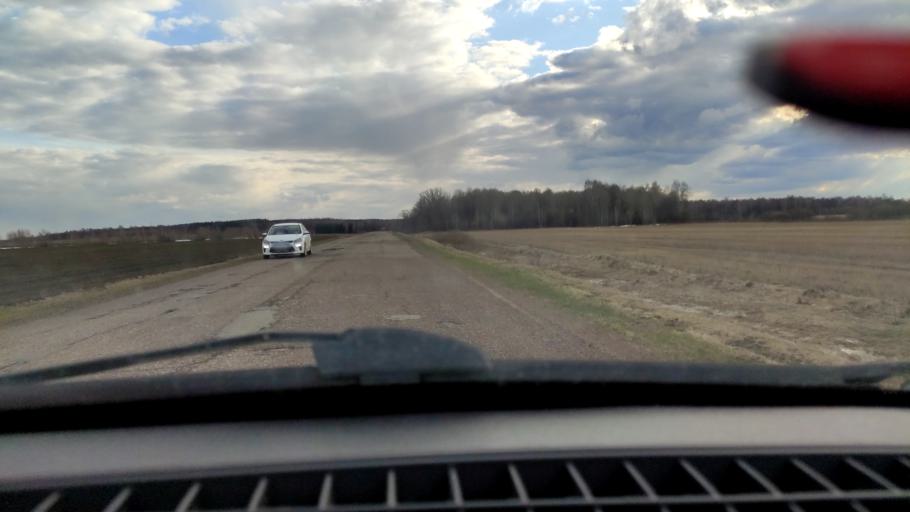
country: RU
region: Bashkortostan
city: Karmaskaly
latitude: 54.3259
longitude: 55.9868
